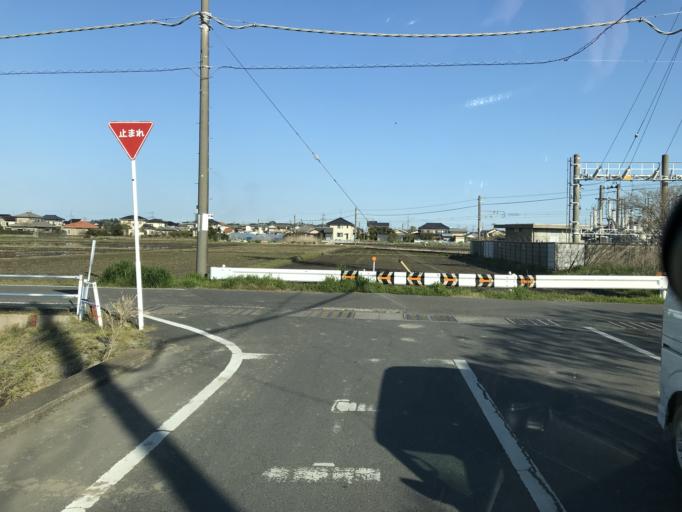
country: JP
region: Chiba
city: Omigawa
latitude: 35.8473
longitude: 140.6115
